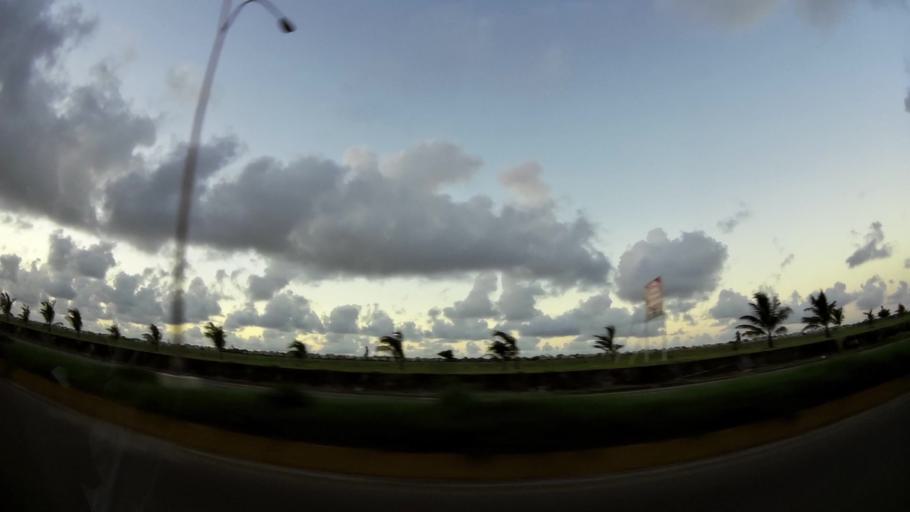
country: GY
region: Demerara-Mahaica
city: Georgetown
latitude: 6.8229
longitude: -58.1039
